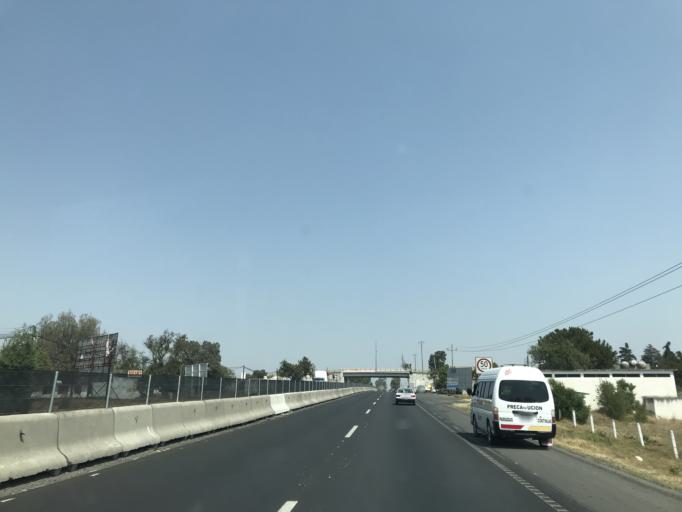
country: MX
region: Tlaxcala
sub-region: Yauhquemehcan
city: San Francisco Tlacuilohcan
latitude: 19.4005
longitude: -98.1857
